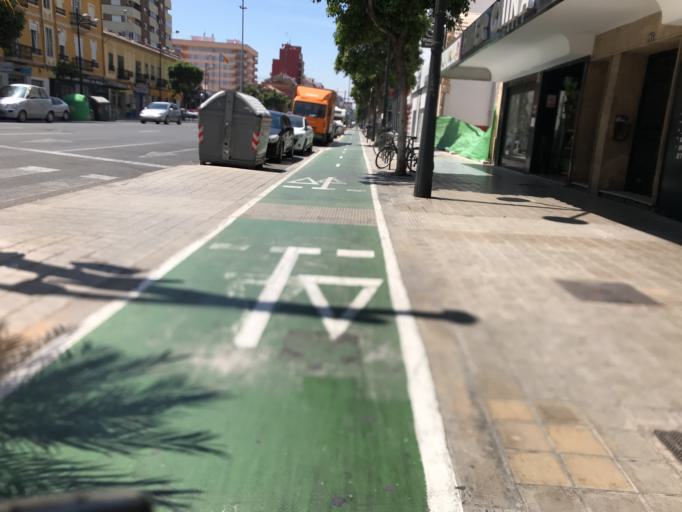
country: ES
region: Valencia
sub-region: Provincia de Valencia
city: Valencia
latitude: 39.4652
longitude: -0.3501
